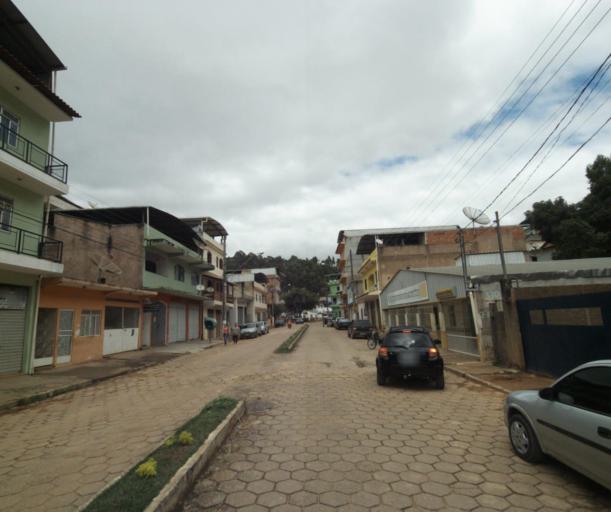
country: BR
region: Espirito Santo
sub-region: Irupi
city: Irupi
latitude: -20.3464
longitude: -41.6432
